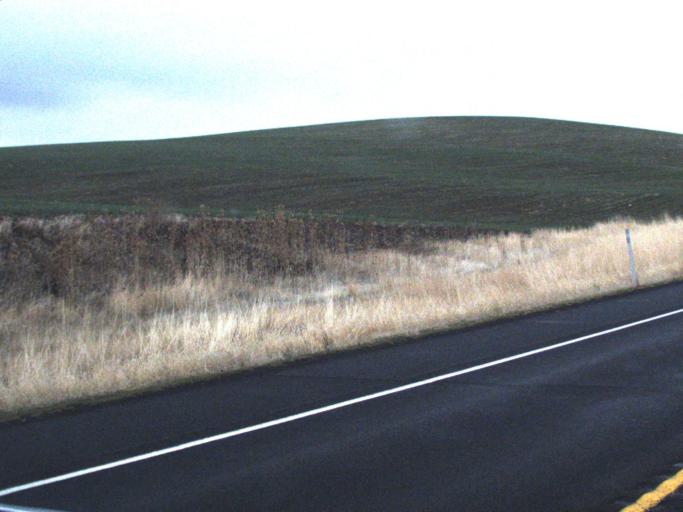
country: US
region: Washington
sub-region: Walla Walla County
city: Walla Walla East
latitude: 46.1302
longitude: -118.1849
